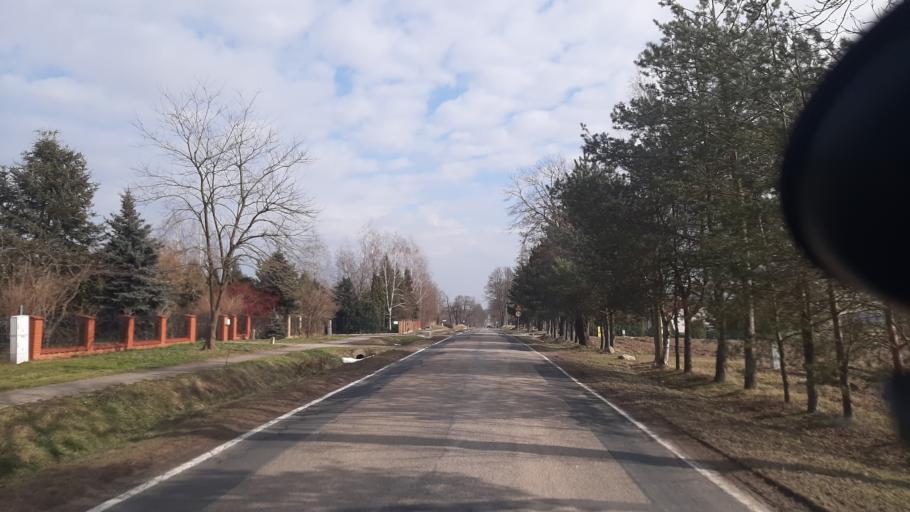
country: PL
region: Lublin Voivodeship
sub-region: Powiat lubelski
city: Niemce
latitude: 51.3606
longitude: 22.5487
